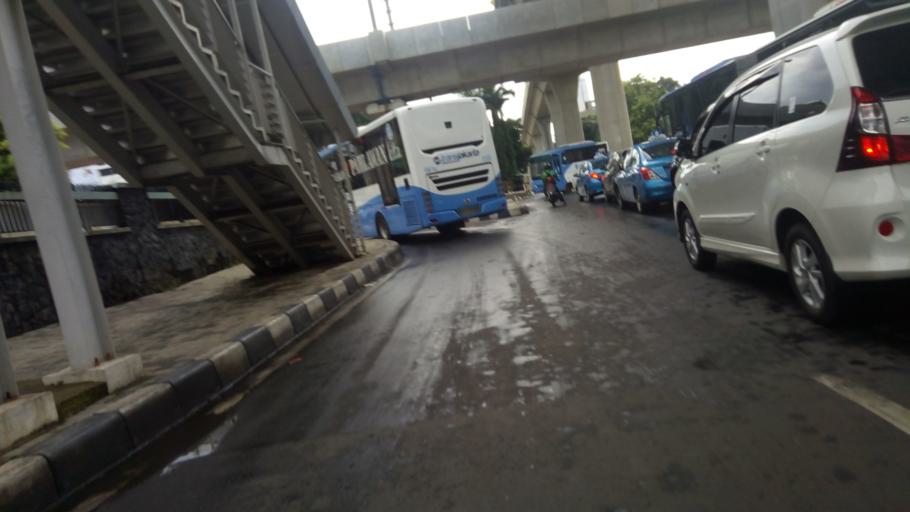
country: ID
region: Jakarta Raya
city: Jakarta
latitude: -6.2400
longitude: 106.7989
